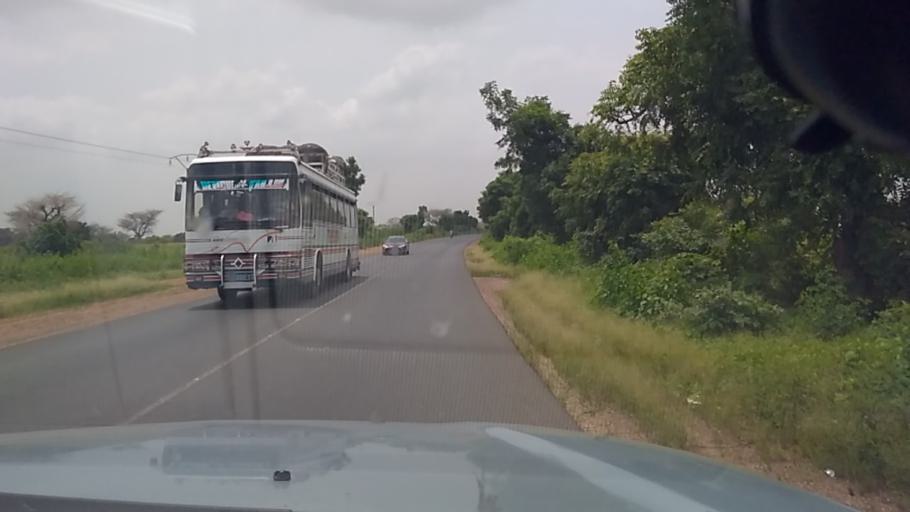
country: SN
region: Thies
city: Mekhe
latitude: 14.9909
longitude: -16.7521
